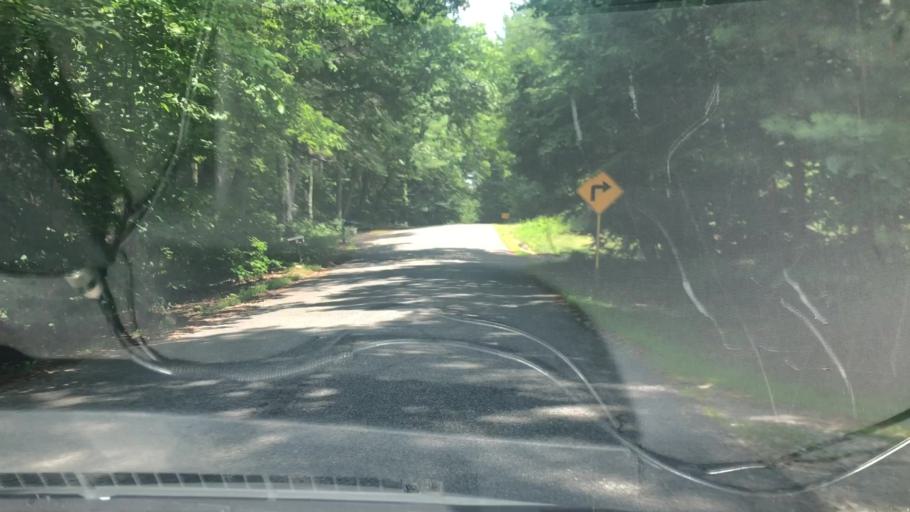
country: US
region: New Hampshire
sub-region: Hillsborough County
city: Mont Vernon
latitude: 42.8768
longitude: -71.6345
